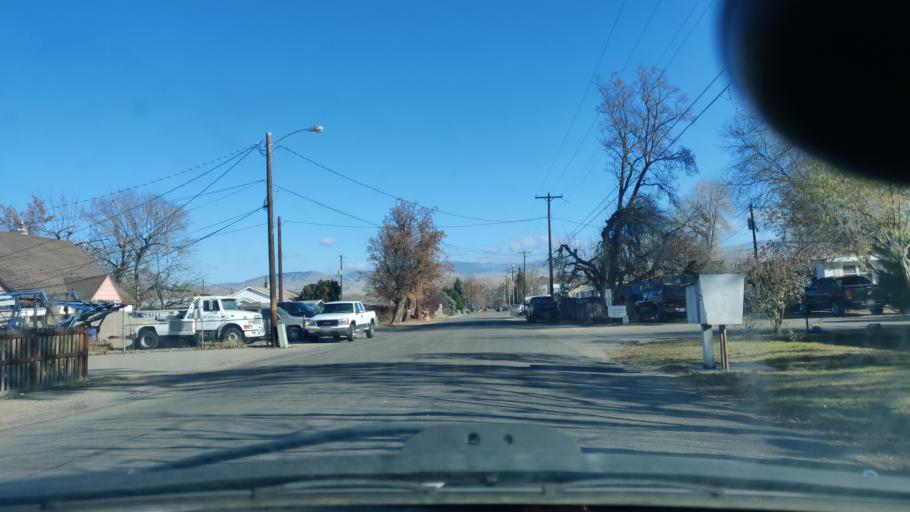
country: US
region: Idaho
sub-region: Ada County
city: Garden City
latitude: 43.6314
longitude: -116.2477
